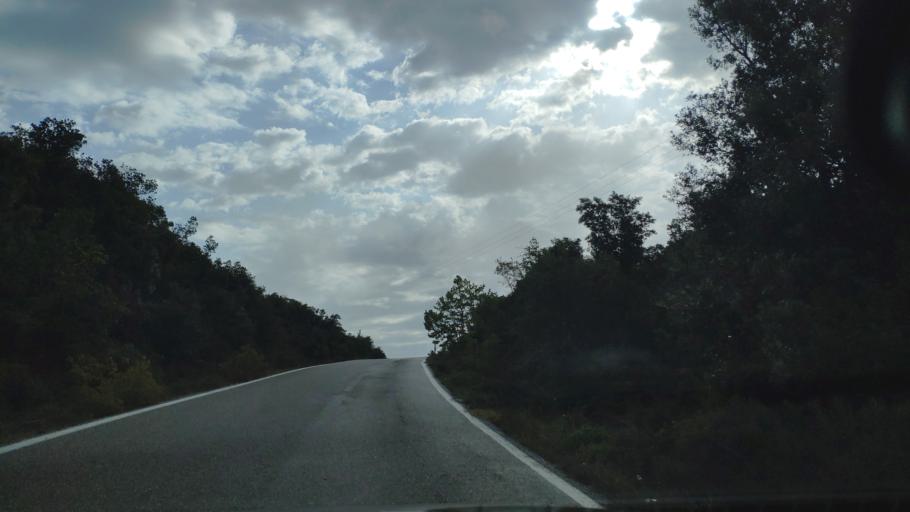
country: GR
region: West Greece
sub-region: Nomos Aitolias kai Akarnanias
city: Sardinia
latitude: 38.8769
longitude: 21.2661
